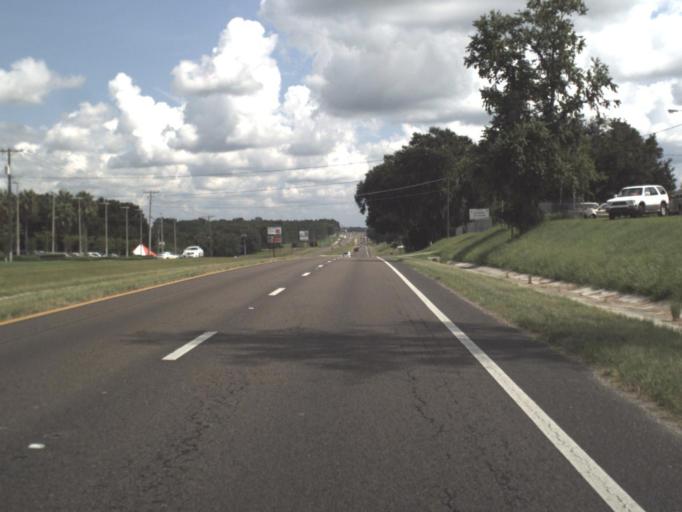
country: US
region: Florida
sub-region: Pasco County
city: Dade City
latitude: 28.3130
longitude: -82.1875
